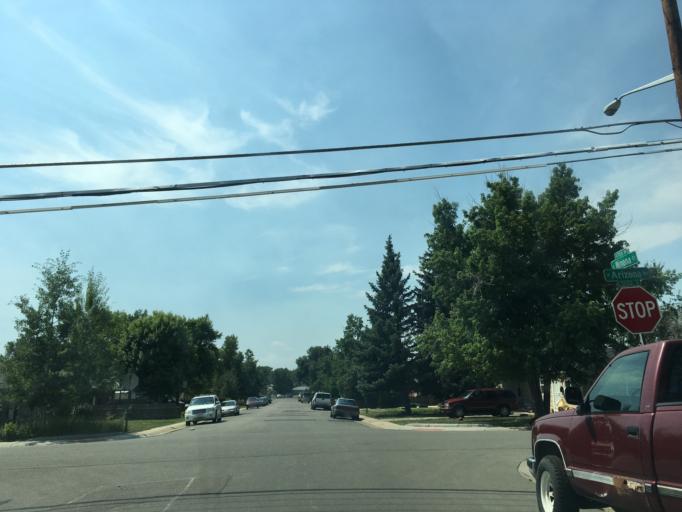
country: US
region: Colorado
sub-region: Jefferson County
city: Lakewood
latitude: 39.6952
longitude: -105.0473
